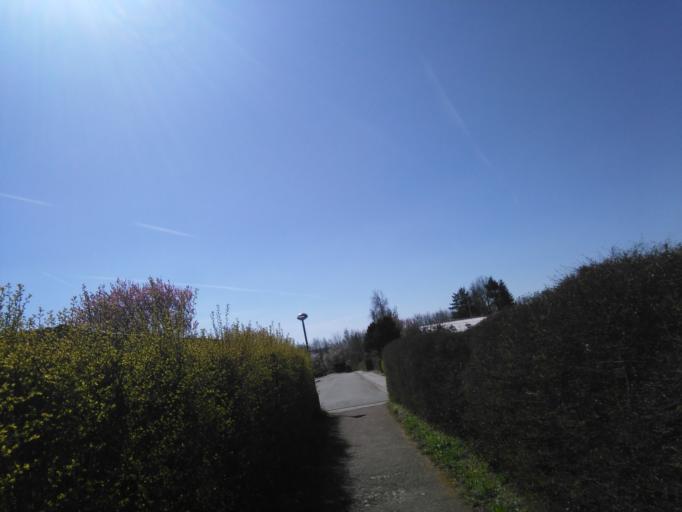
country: DK
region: Central Jutland
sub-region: Arhus Kommune
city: Marslet
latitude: 56.0734
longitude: 10.1563
